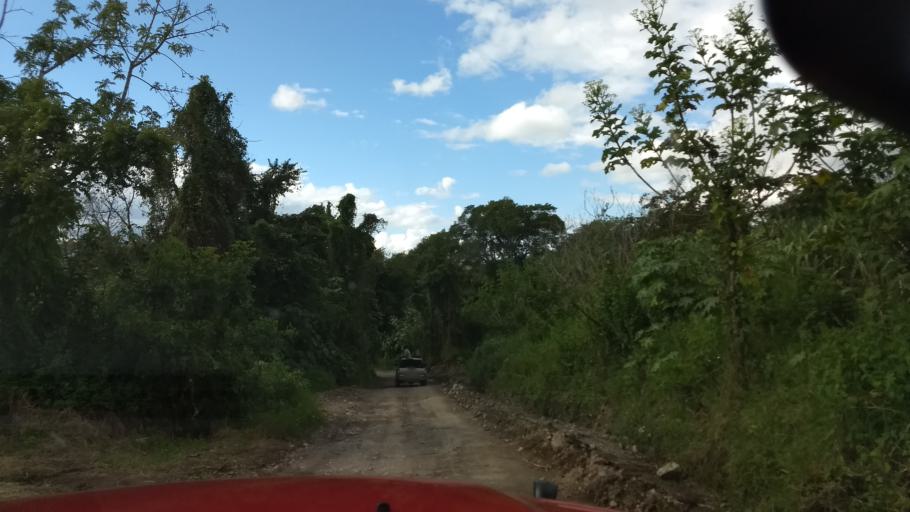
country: MX
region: Colima
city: Suchitlan
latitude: 19.4642
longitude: -103.7506
